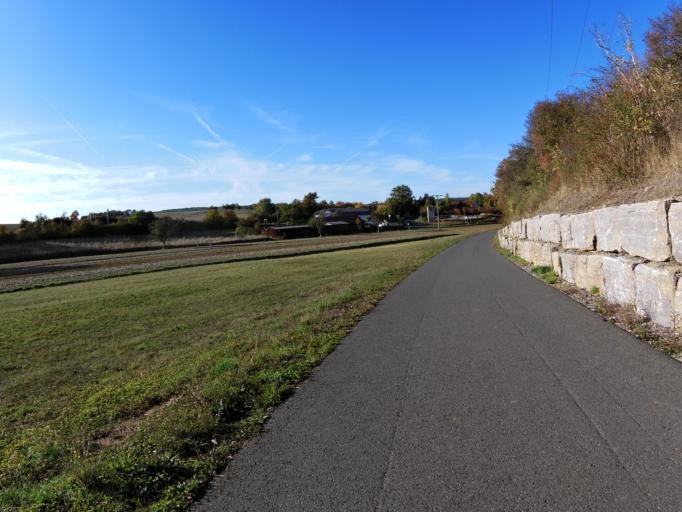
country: DE
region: Bavaria
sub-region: Regierungsbezirk Unterfranken
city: Reichenberg
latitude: 49.7205
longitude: 9.9179
